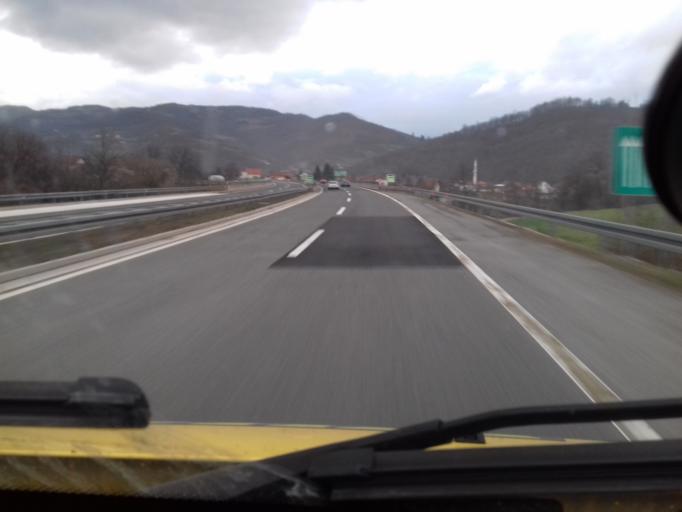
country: BA
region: Federation of Bosnia and Herzegovina
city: Ilijas
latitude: 43.9506
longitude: 18.2545
